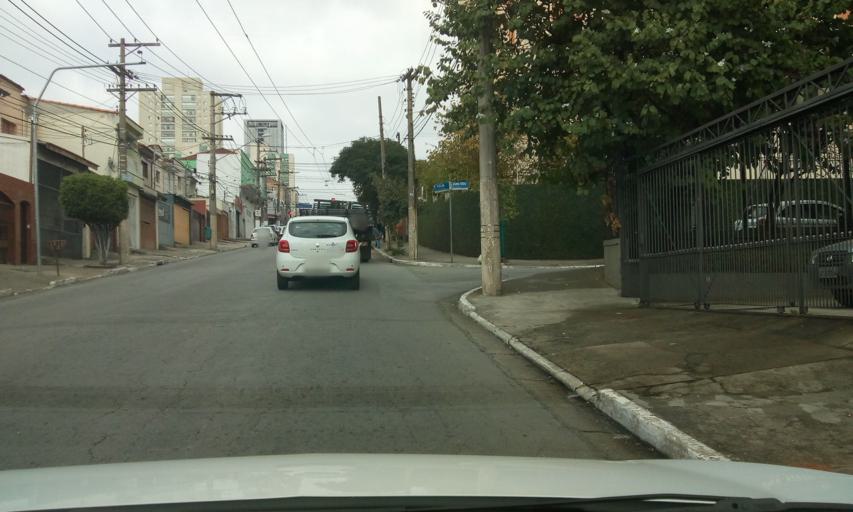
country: BR
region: Sao Paulo
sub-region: Sao Paulo
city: Sao Paulo
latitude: -23.5589
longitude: -46.5865
